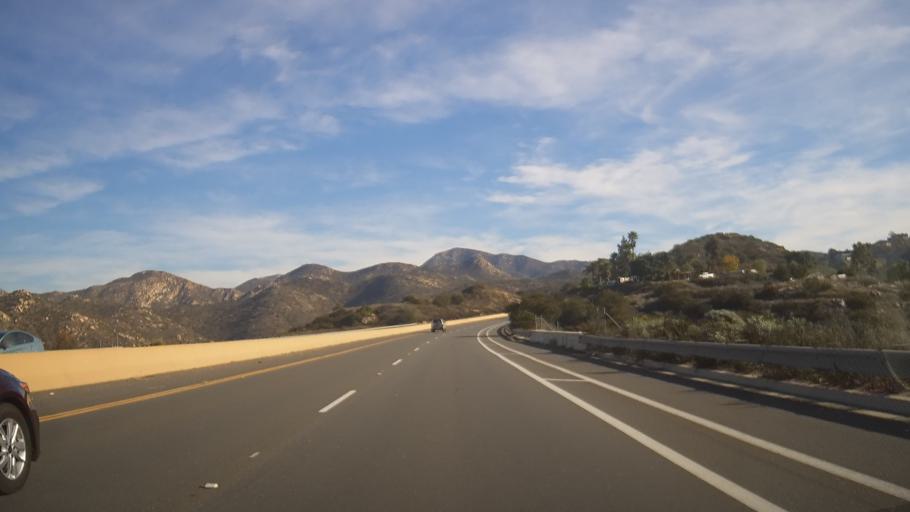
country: US
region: California
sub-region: San Diego County
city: Poway
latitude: 32.9463
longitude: -117.0037
